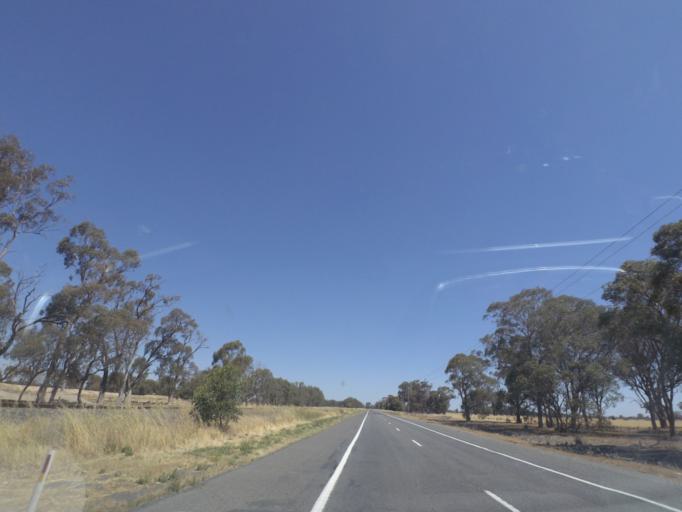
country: AU
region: Victoria
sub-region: Greater Shepparton
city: Shepparton
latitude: -36.2169
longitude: 145.4318
